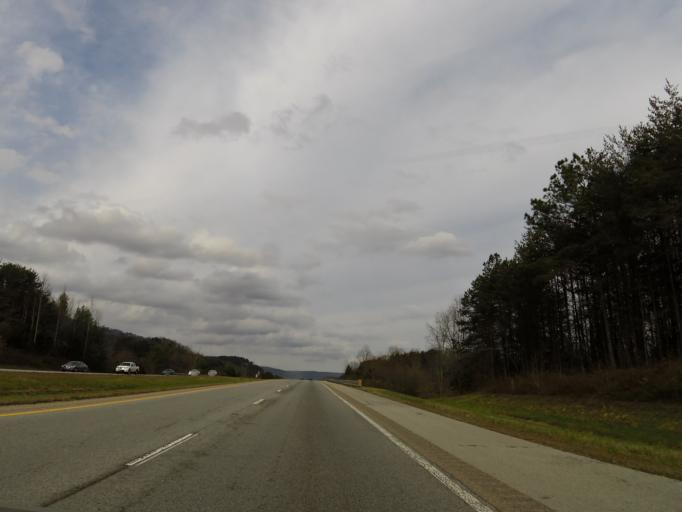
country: US
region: Tennessee
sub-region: Hamilton County
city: Walden
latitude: 35.1429
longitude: -85.2925
